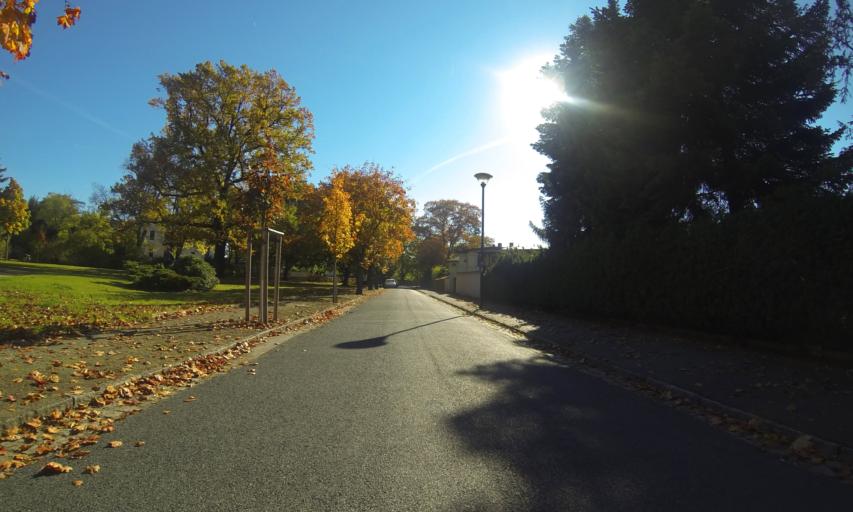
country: DE
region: Saxony
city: Radebeul
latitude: 51.1086
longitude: 13.6629
